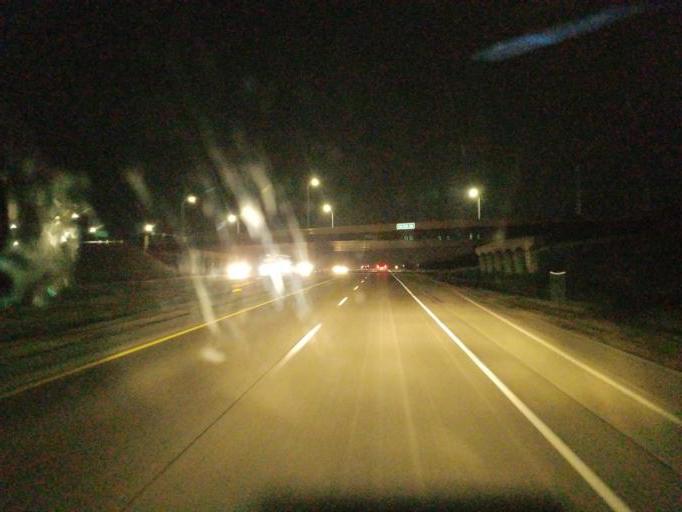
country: US
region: Iowa
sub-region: Dallas County
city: Waukee
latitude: 41.5686
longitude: -93.8547
